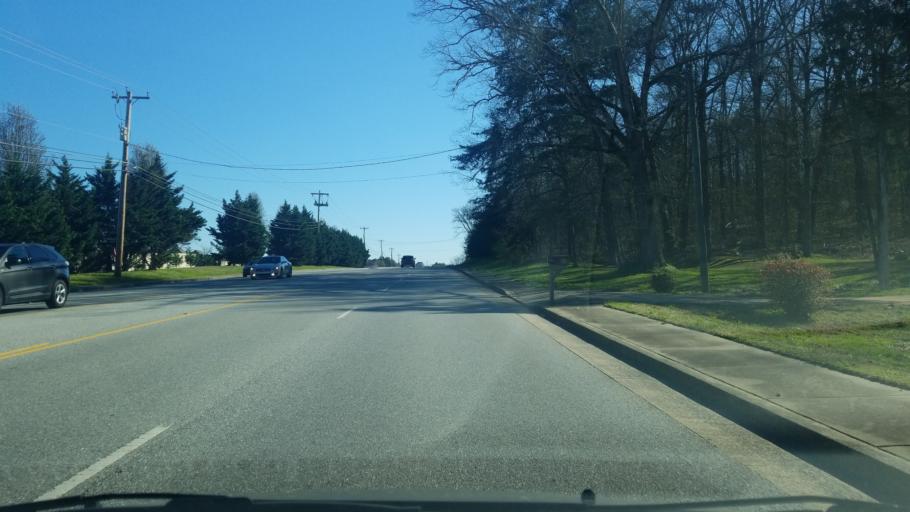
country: US
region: Tennessee
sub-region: Hamilton County
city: Middle Valley
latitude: 35.1685
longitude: -85.1830
